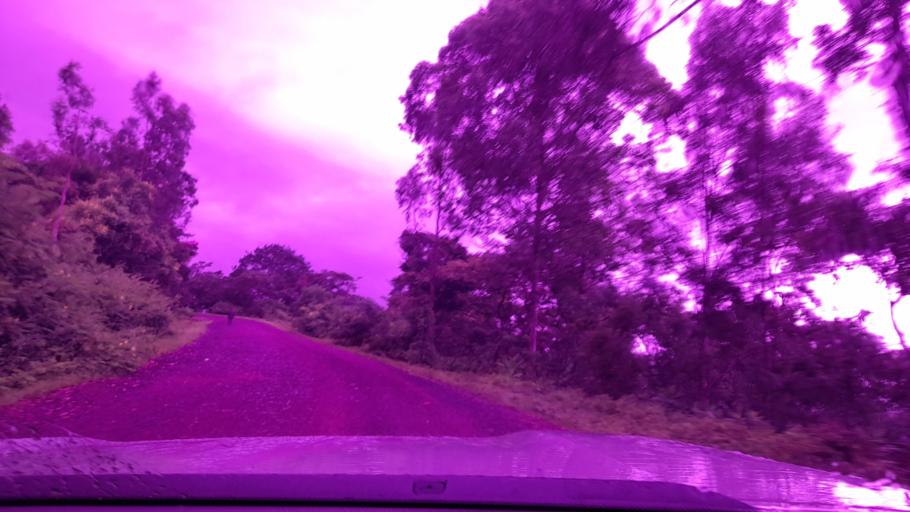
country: ET
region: Oromiya
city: Metu
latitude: 8.4431
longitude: 35.6247
